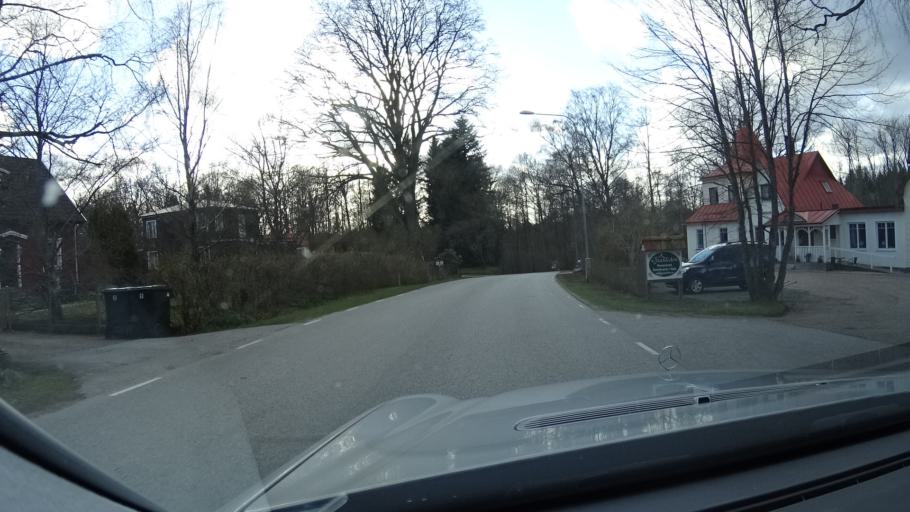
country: SE
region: Skane
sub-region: Hoors Kommun
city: Satofta
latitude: 55.9031
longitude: 13.5991
